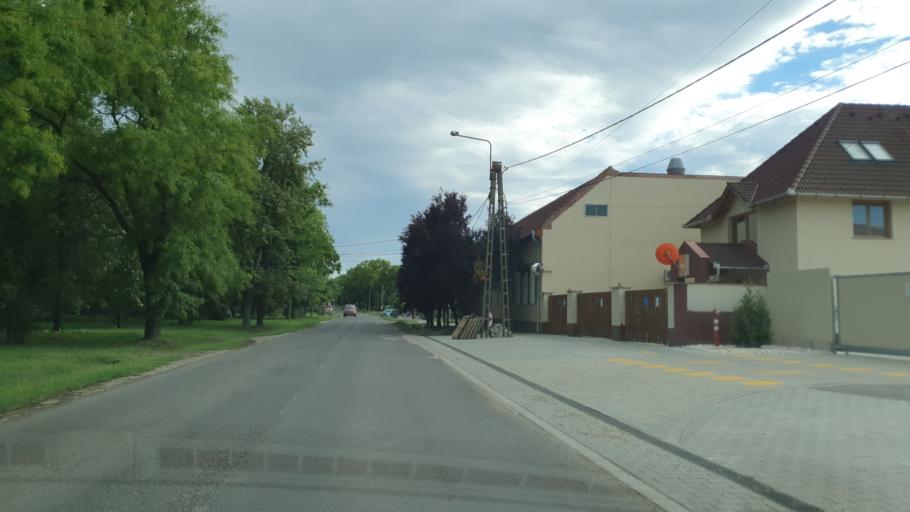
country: HU
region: Heves
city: Lorinci
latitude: 47.7455
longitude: 19.6790
